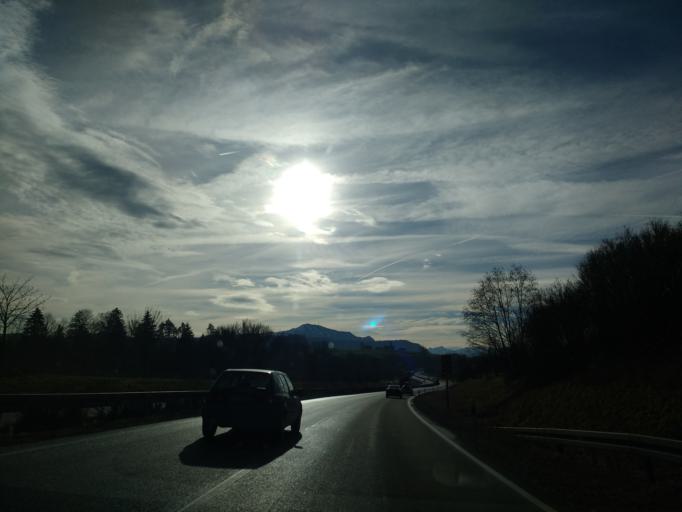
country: DE
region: Bavaria
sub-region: Swabia
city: Waltenhofen
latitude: 47.6646
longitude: 10.2992
